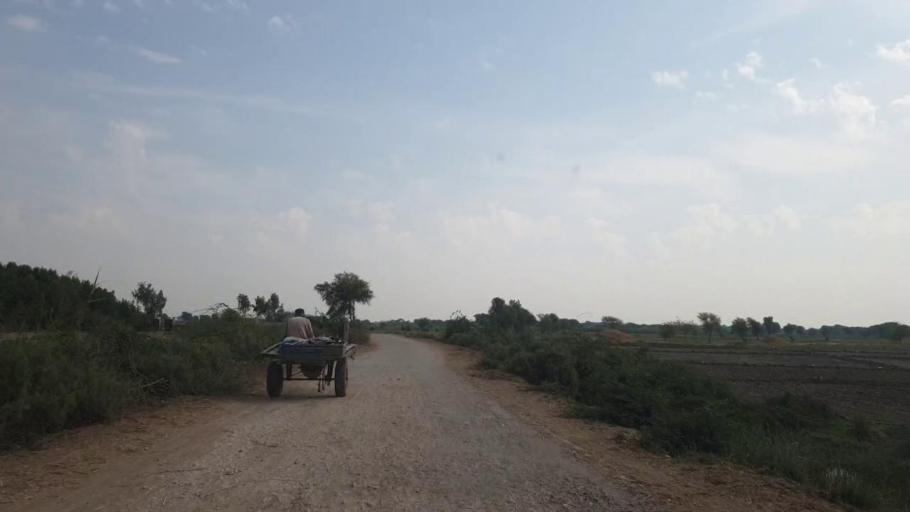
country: PK
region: Sindh
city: Rajo Khanani
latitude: 24.9586
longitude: 69.0073
